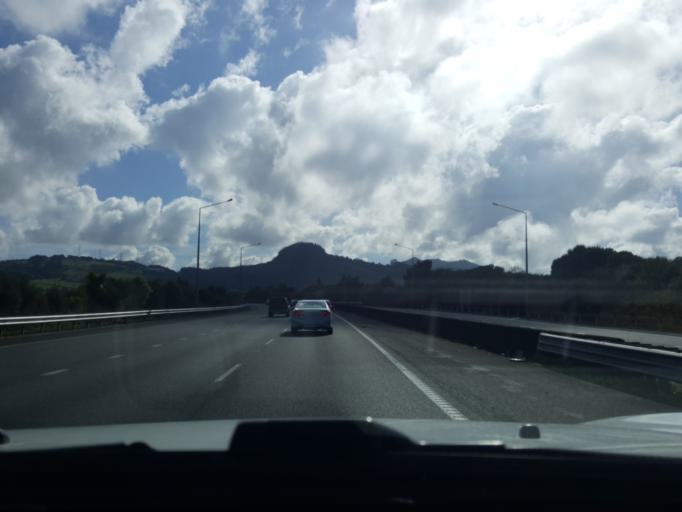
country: NZ
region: Auckland
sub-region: Auckland
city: Pukekohe East
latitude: -37.2366
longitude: 175.0203
